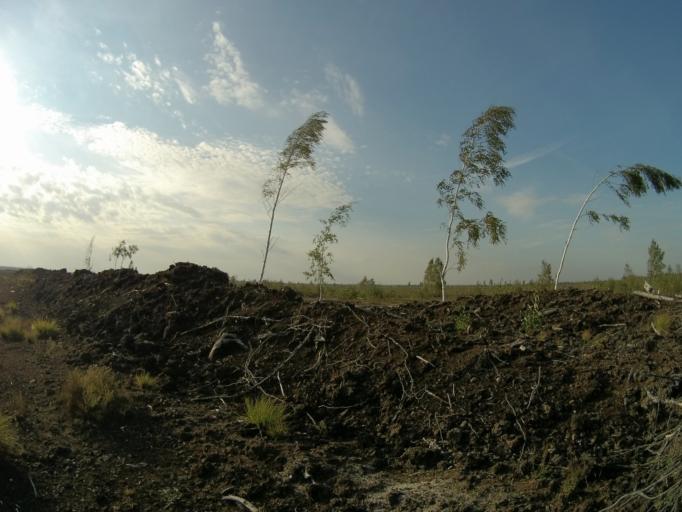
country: RU
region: Vladimir
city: Urshel'skiy
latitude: 55.8007
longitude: 40.1168
